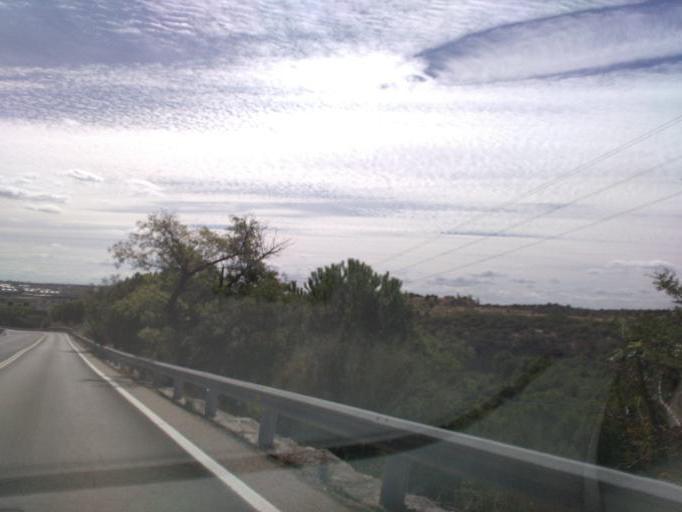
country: ES
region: Madrid
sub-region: Provincia de Madrid
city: Torrelodones
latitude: 40.5333
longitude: -3.9503
